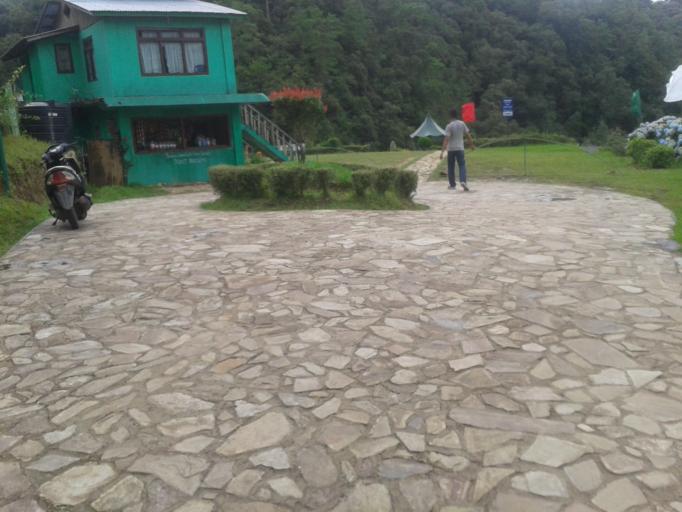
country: IN
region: Meghalaya
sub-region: East Khasi Hills
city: Shillong
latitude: 25.5389
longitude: 91.8219
